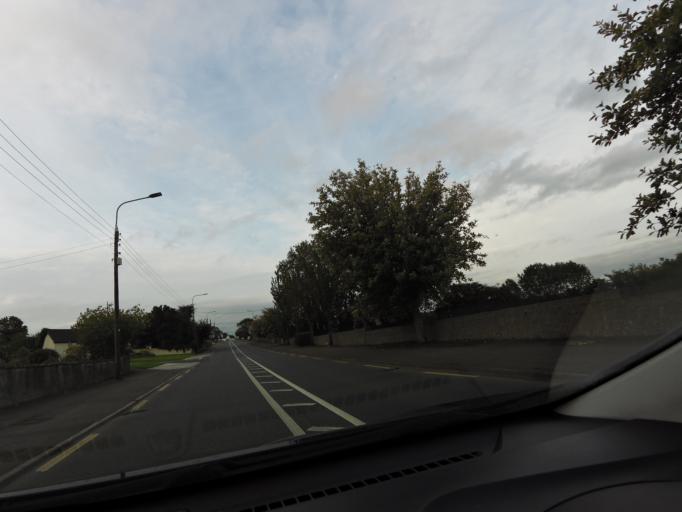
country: IE
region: Leinster
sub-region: Uibh Fhaili
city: Ferbane
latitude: 53.2761
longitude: -7.8259
